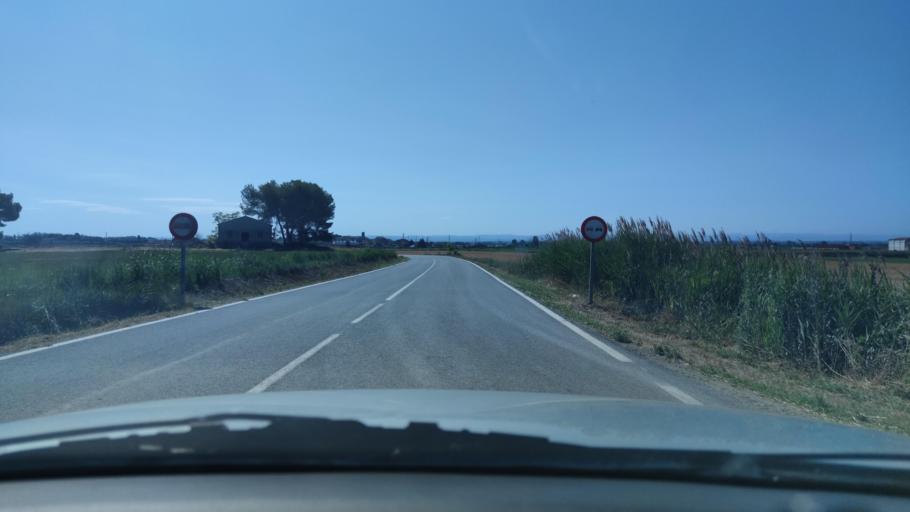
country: ES
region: Catalonia
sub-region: Provincia de Lleida
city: Penelles
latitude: 41.7532
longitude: 0.9746
